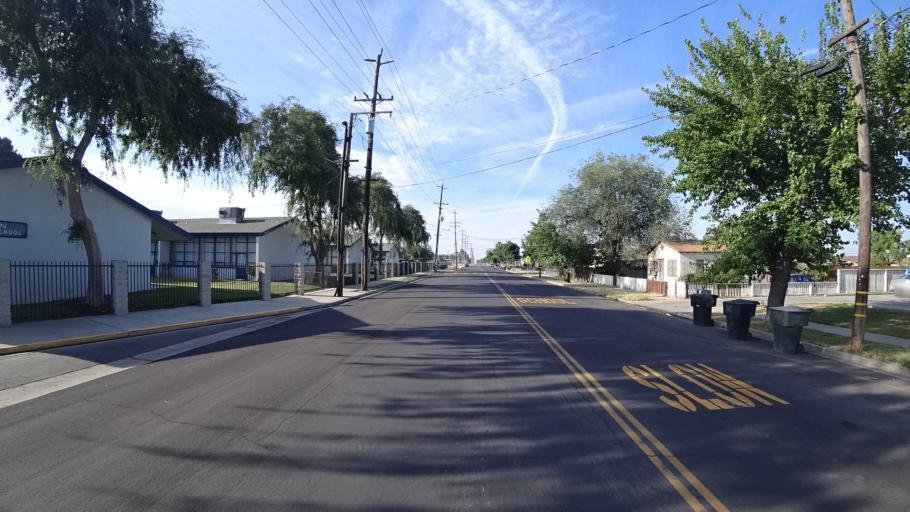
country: US
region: California
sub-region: Kings County
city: Hanford
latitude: 36.3154
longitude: -119.6459
